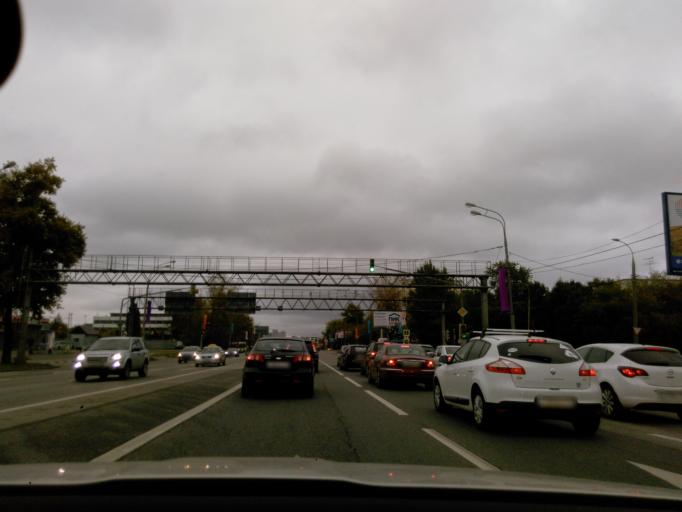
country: RU
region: Moscow
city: Strogino
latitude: 55.8302
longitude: 37.4073
